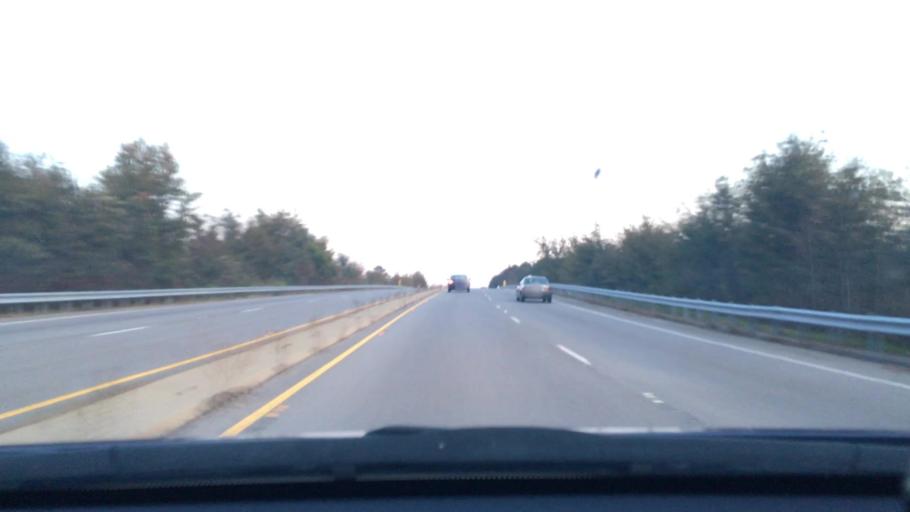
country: US
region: South Carolina
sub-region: Richland County
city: Gadsden
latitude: 33.9427
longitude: -80.6894
